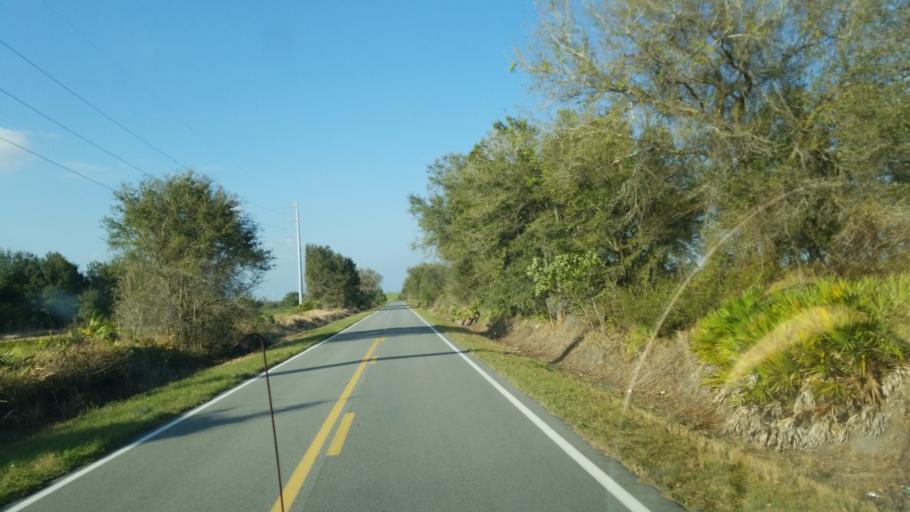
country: US
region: Florida
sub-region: Polk County
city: Mulberry
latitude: 27.7588
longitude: -81.9723
